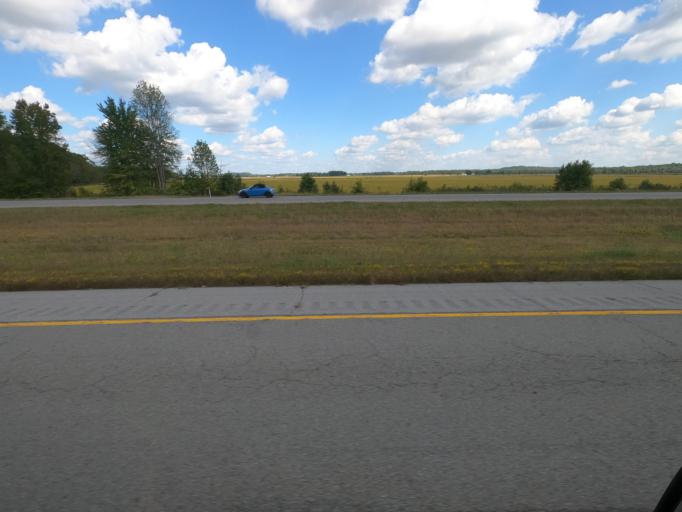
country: US
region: Illinois
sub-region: Massac County
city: Metropolis
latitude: 37.3113
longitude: -88.7570
